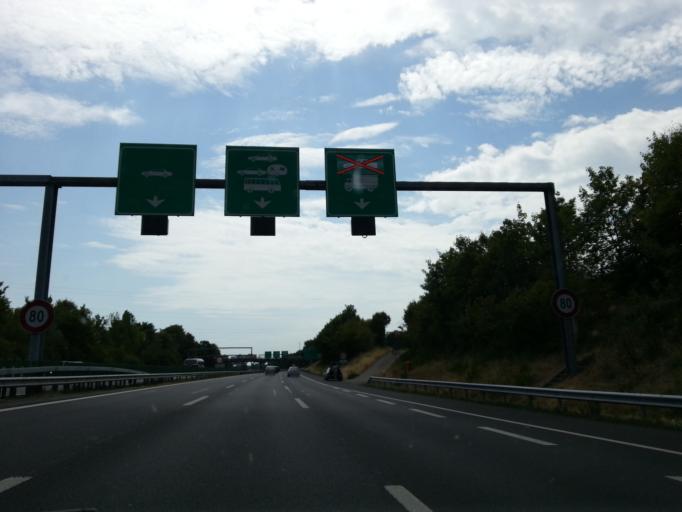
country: FR
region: Rhone-Alpes
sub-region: Departement de la Haute-Savoie
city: Saint-Julien-en-Genevois
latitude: 46.1556
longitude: 6.0998
